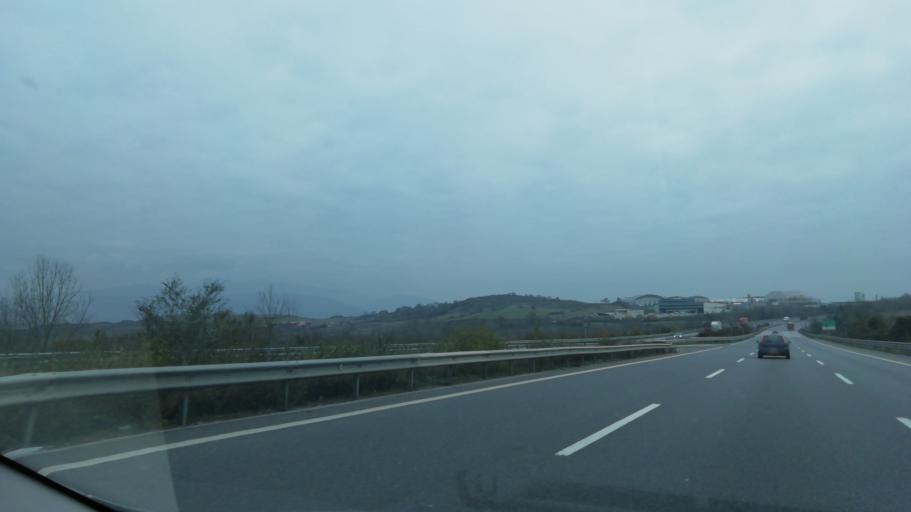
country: TR
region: Duzce
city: Gumusova
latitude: 40.8407
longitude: 30.9699
